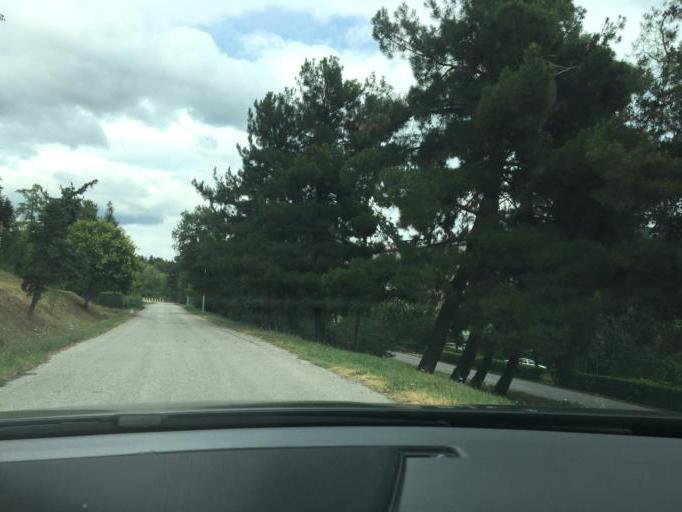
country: MK
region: Cair
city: Cair
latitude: 42.0005
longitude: 21.4521
